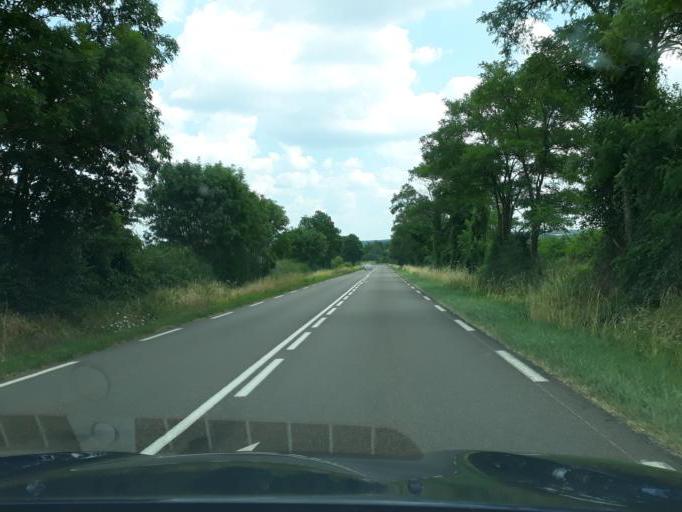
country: FR
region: Centre
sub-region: Departement du Cher
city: Nerondes
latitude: 46.9991
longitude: 2.7841
